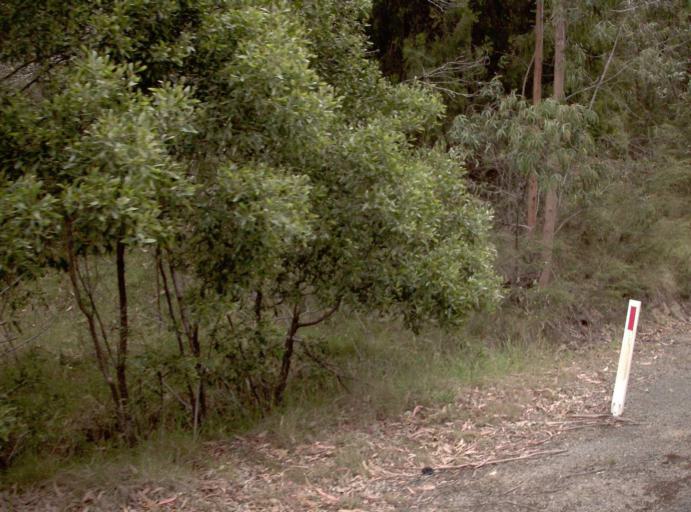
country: AU
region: New South Wales
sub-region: Bombala
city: Bombala
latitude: -37.2871
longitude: 149.2223
